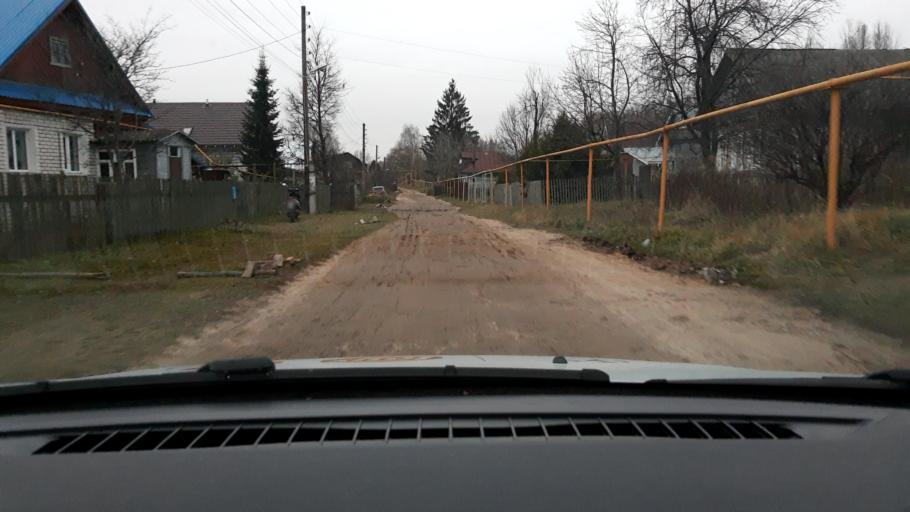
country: RU
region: Nizjnij Novgorod
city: Neklyudovo
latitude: 56.4212
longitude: 44.0192
